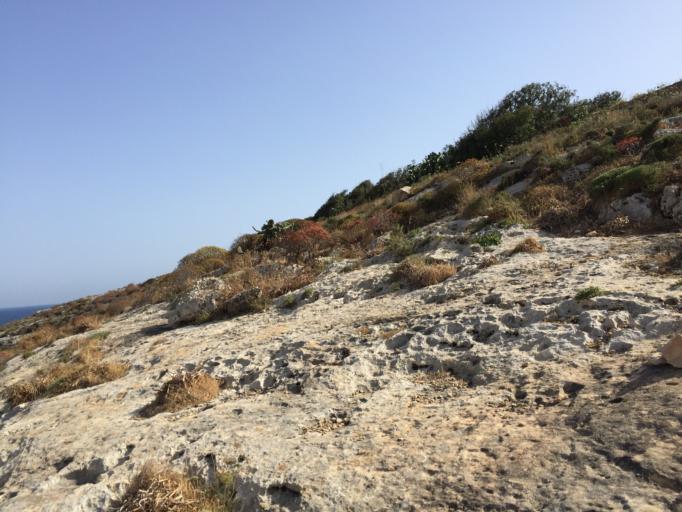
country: MT
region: Ghajnsielem
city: Ghajnsielem
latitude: 36.0192
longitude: 14.2717
